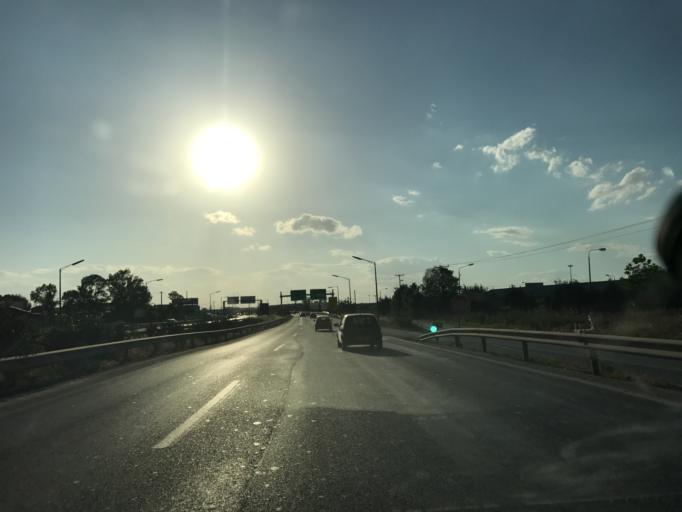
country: GR
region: Central Macedonia
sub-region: Nomos Thessalonikis
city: Menemeni
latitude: 40.6547
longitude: 22.8950
